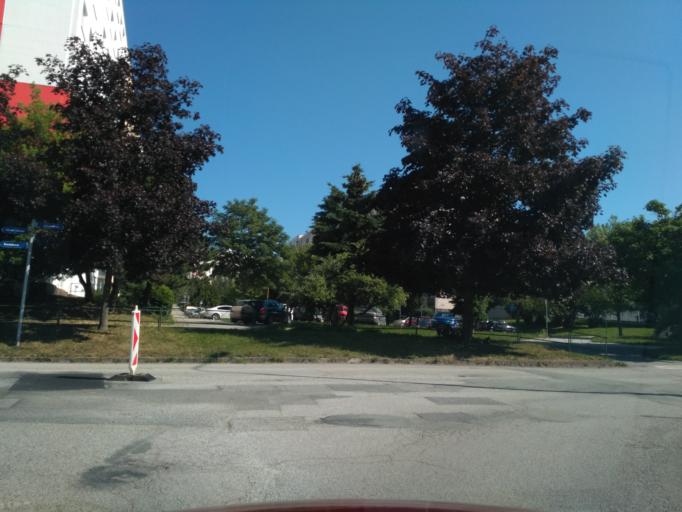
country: SK
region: Kosicky
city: Kosice
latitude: 48.7123
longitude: 21.2126
